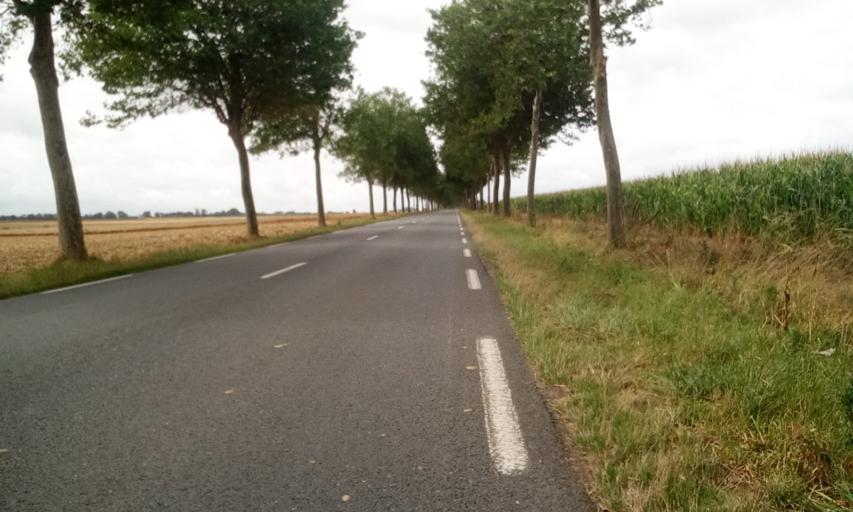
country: FR
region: Lower Normandy
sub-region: Departement du Calvados
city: Cheux
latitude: 49.1730
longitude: -0.5492
